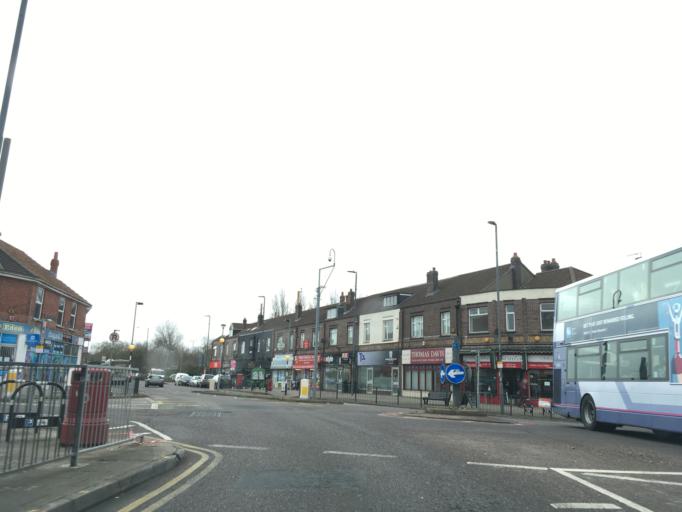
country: GB
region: England
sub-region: South Gloucestershire
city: Stoke Gifford
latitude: 51.5018
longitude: -2.5793
